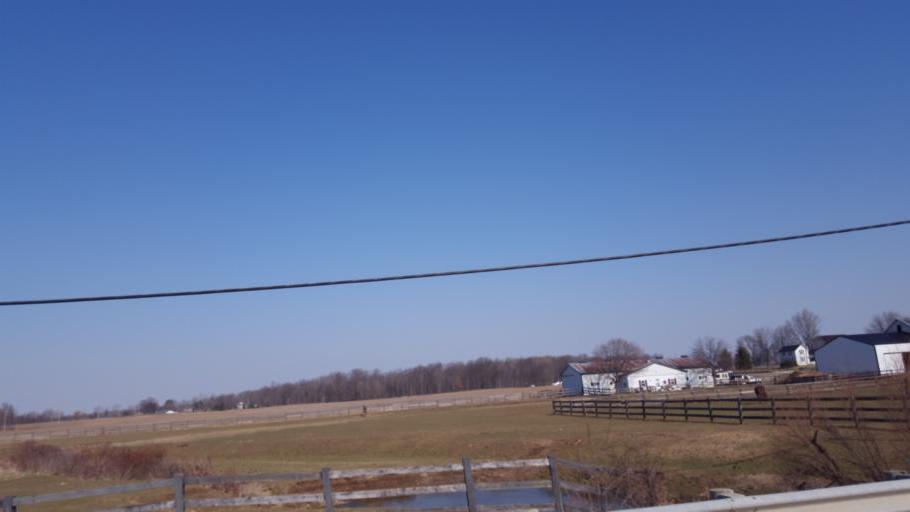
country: US
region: Ohio
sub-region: Crawford County
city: Galion
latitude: 40.7333
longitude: -82.7428
